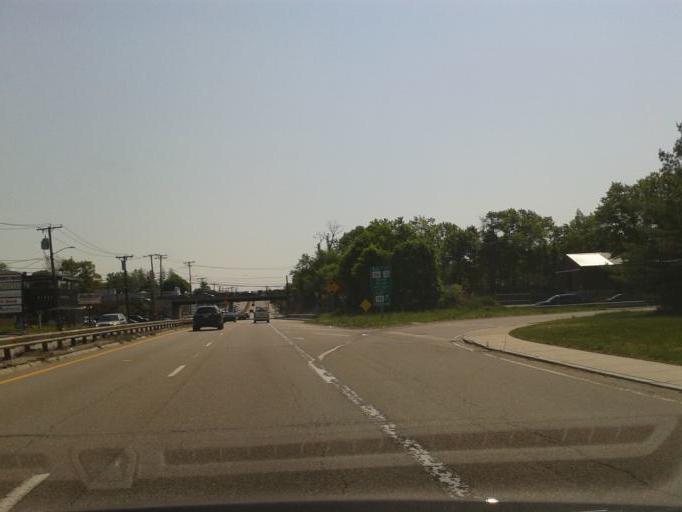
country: US
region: Massachusetts
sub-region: Middlesex County
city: Framingham
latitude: 42.2980
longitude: -71.4108
